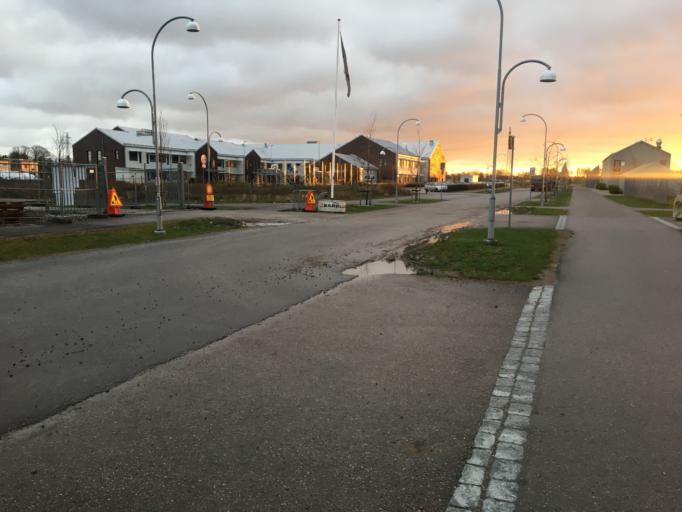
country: SE
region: Skane
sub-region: Staffanstorps Kommun
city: Hjaerup
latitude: 55.6700
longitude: 13.1529
